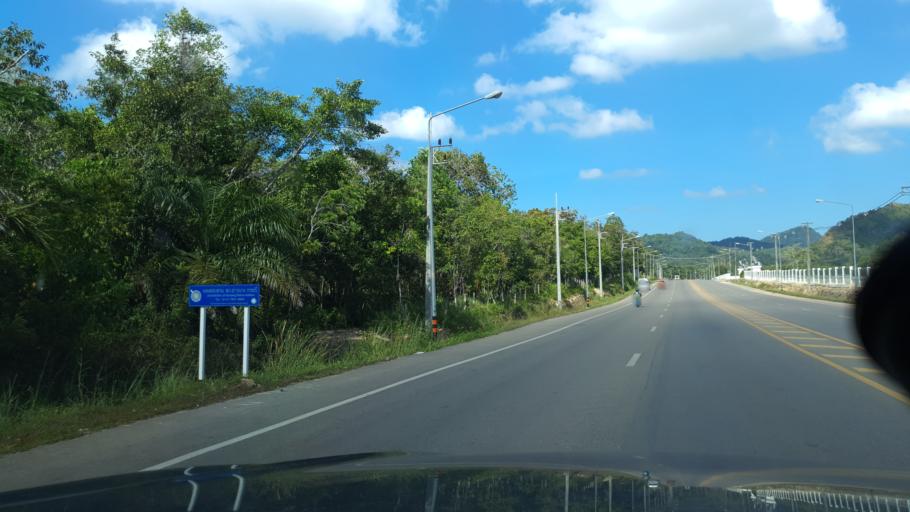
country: TH
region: Phangnga
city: Ban Ao Nang
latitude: 8.0388
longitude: 98.8522
